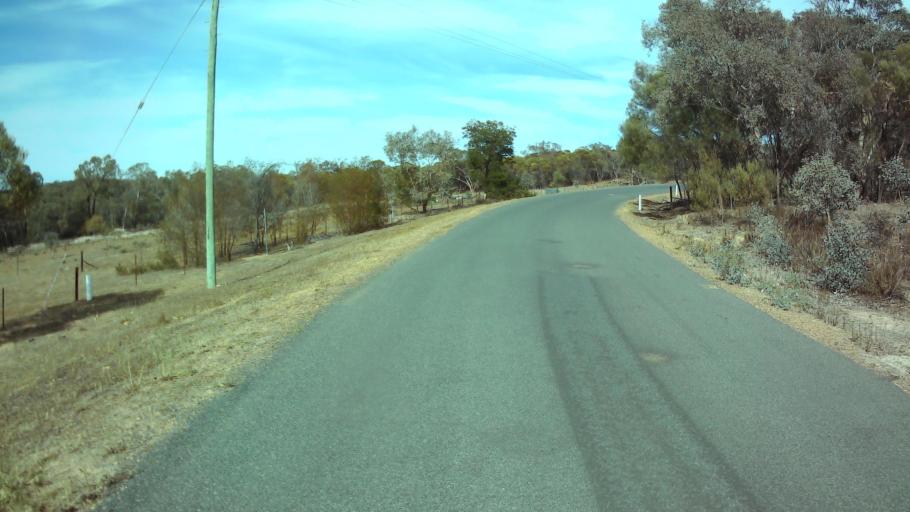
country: AU
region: New South Wales
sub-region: Weddin
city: Grenfell
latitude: -33.8793
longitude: 148.1953
